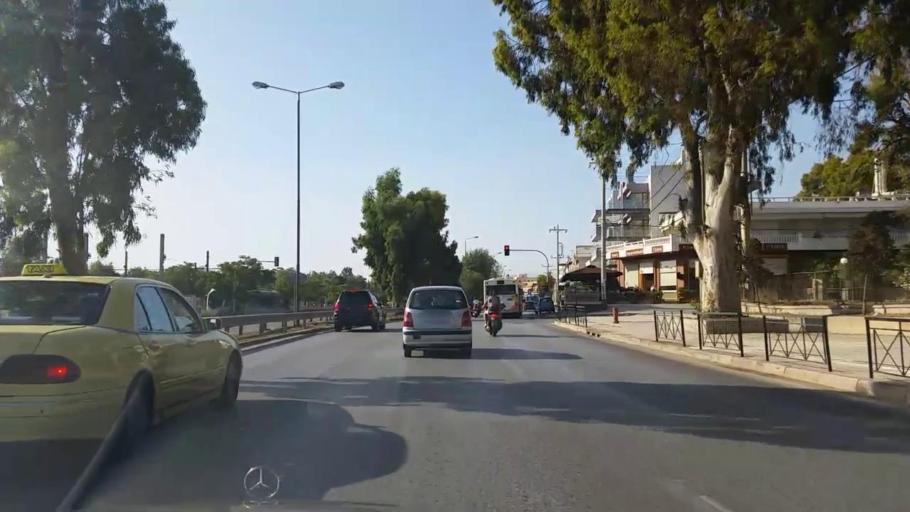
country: GR
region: Attica
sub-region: Nomarchia Athinas
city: Glyfada
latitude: 37.8487
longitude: 23.7532
